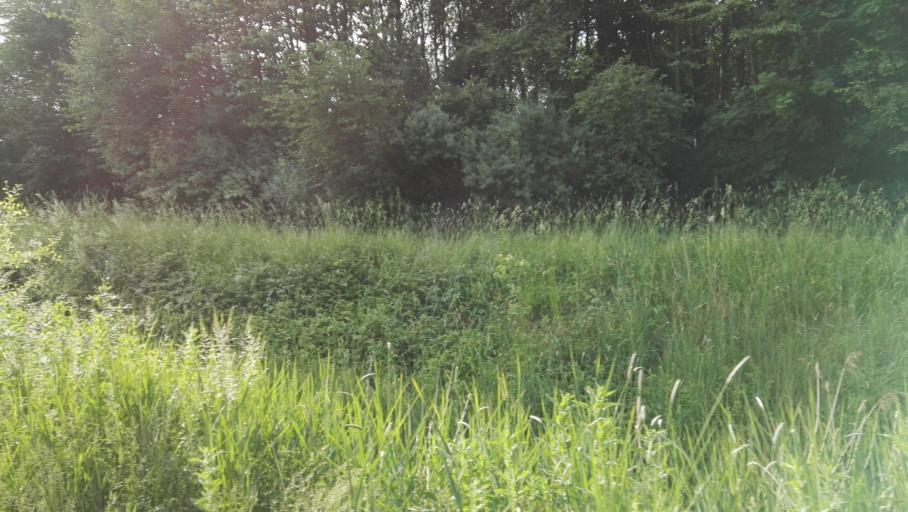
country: DK
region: Capital Region
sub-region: Ballerup Kommune
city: Ballerup
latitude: 55.7100
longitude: 12.3561
